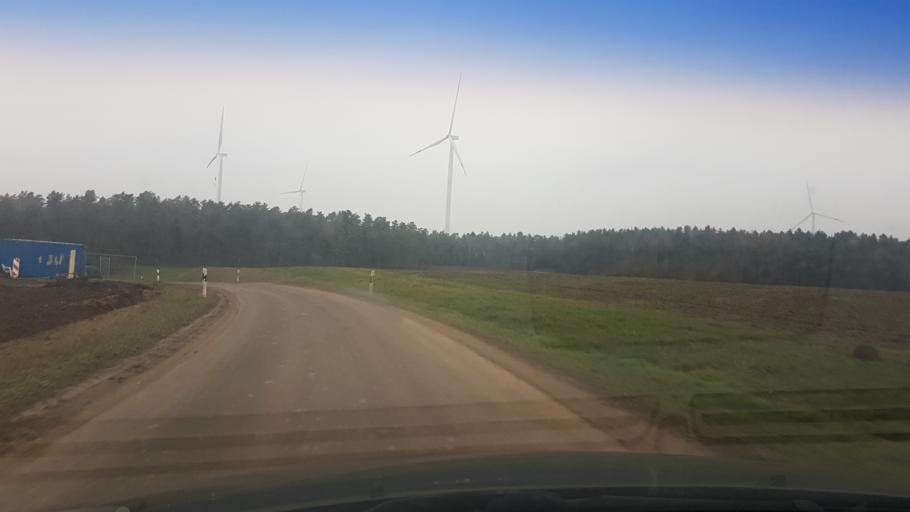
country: DE
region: Bavaria
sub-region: Upper Franconia
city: Kasendorf
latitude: 50.0381
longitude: 11.2924
